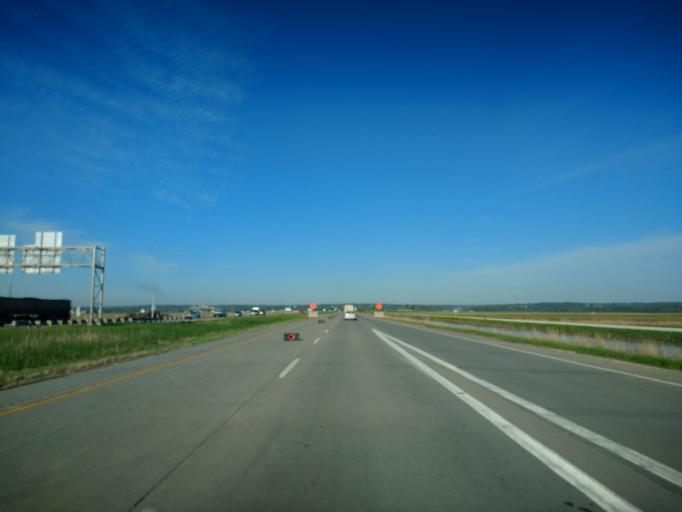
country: US
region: Iowa
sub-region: Pottawattamie County
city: Carter Lake
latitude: 41.3529
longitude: -95.9060
